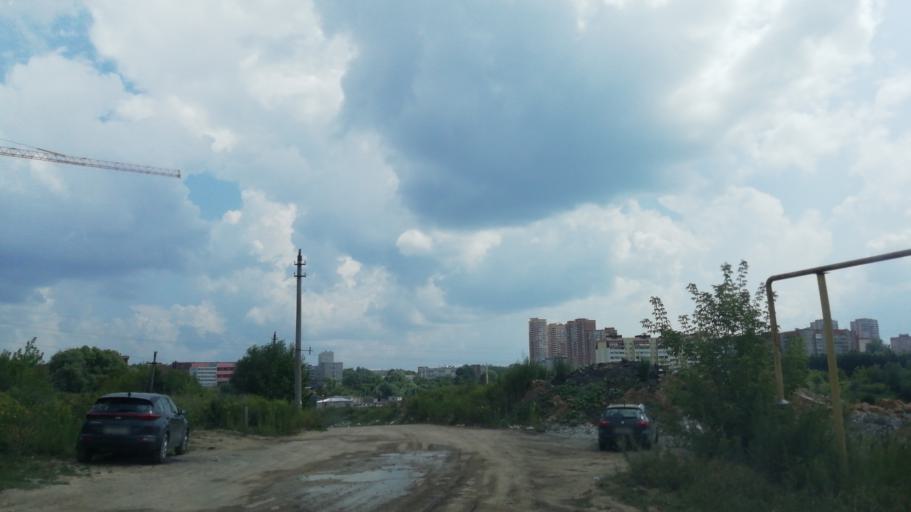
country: RU
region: Tula
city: Mendeleyevskiy
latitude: 54.1607
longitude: 37.5716
